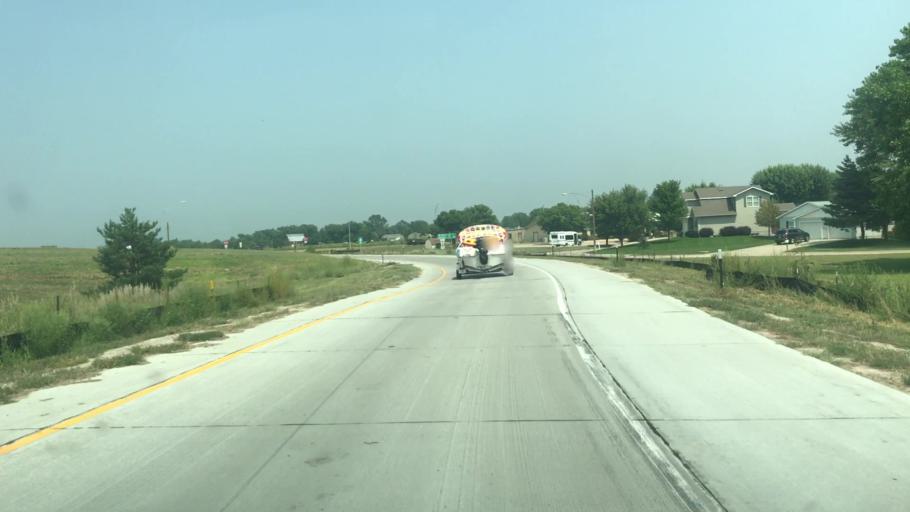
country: US
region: Nebraska
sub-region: Hall County
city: Grand Island
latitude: 40.9513
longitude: -98.3835
